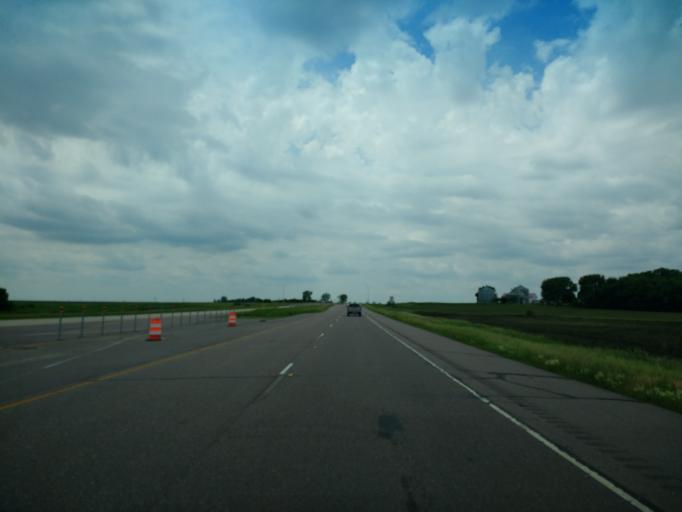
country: US
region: Minnesota
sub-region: Cottonwood County
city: Mountain Lake
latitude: 43.9311
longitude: -94.9570
